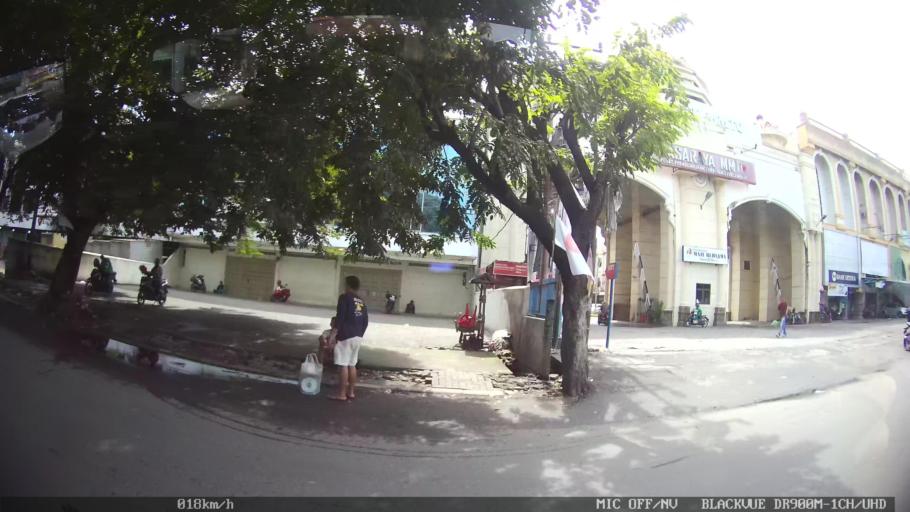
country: ID
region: North Sumatra
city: Medan
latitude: 3.6038
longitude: 98.7069
